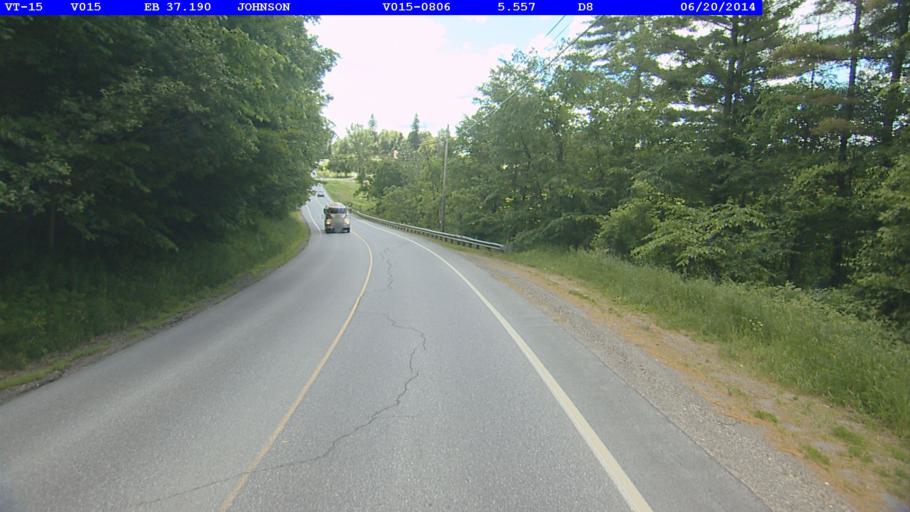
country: US
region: Vermont
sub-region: Lamoille County
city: Johnson
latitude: 44.6201
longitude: -72.6670
